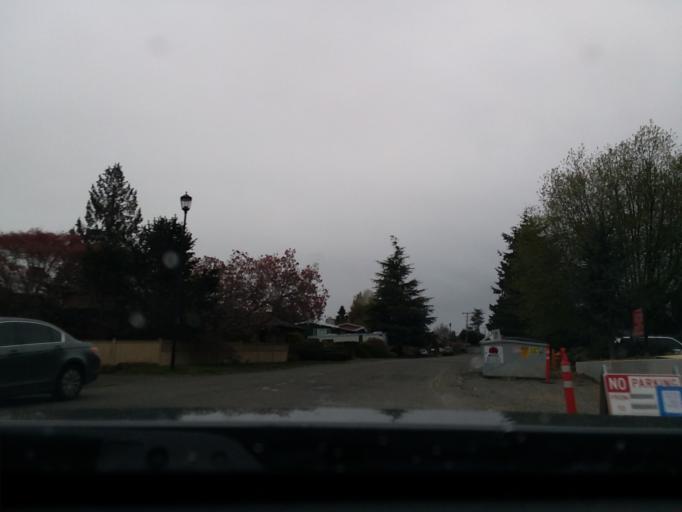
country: US
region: Washington
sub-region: King County
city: Shoreline
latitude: 47.7063
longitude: -122.3715
